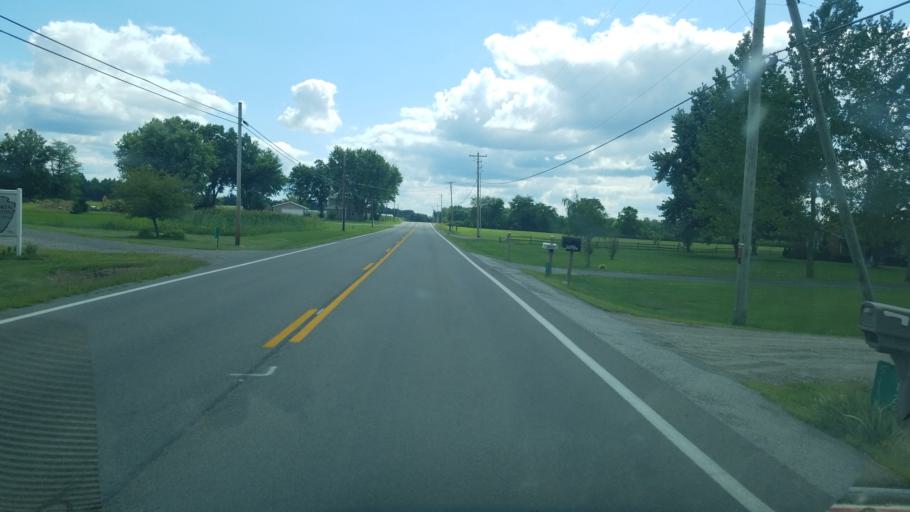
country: US
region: Ohio
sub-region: Allen County
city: Lima
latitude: 40.8120
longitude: -84.0994
